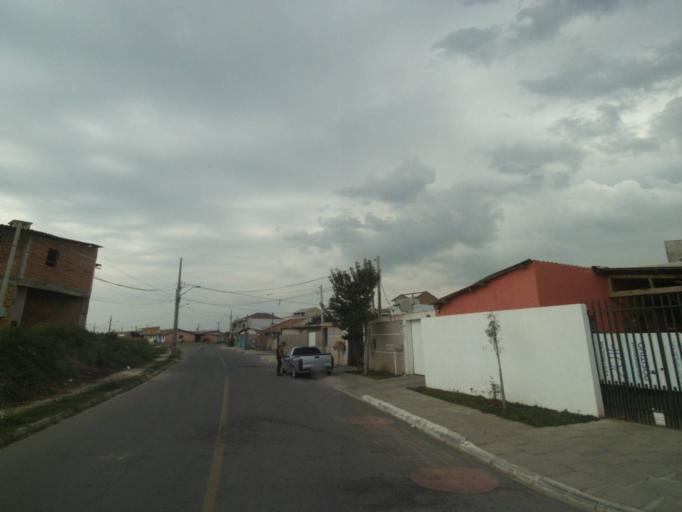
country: BR
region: Parana
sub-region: Sao Jose Dos Pinhais
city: Sao Jose dos Pinhais
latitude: -25.4921
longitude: -49.2001
